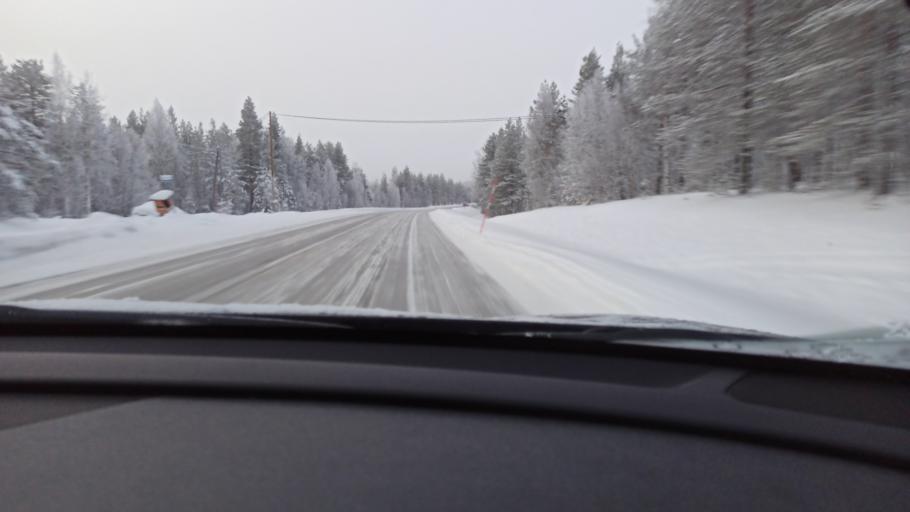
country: FI
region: Lapland
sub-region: Pohjois-Lappi
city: Sodankylae
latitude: 66.9315
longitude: 26.2589
